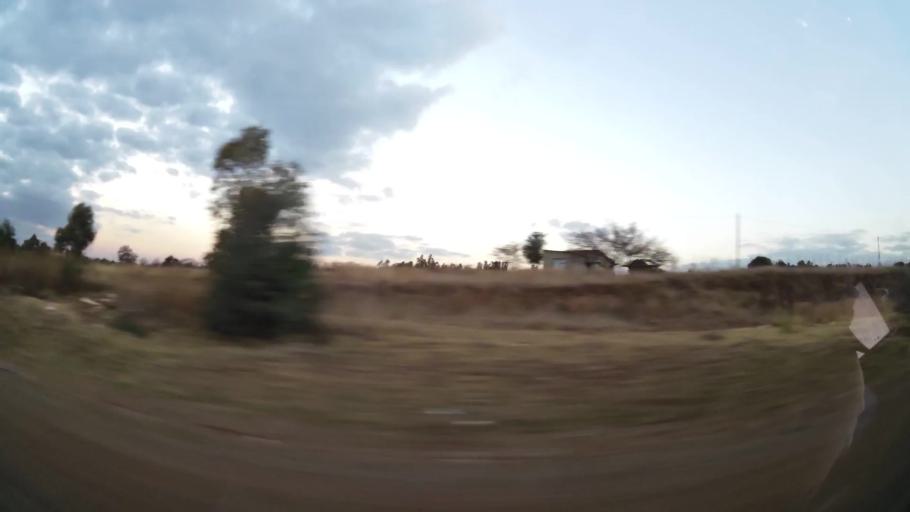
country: ZA
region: Gauteng
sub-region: West Rand District Municipality
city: Krugersdorp
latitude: -26.0658
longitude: 27.6917
